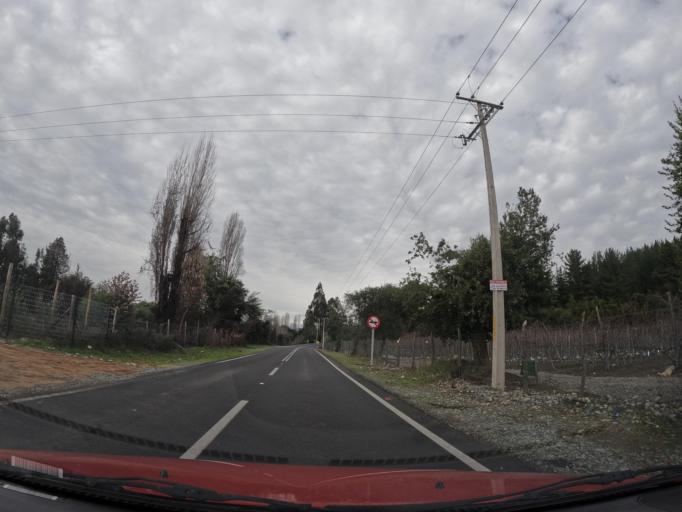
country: CL
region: Maule
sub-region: Provincia de Linares
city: Linares
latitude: -35.9117
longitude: -71.4837
